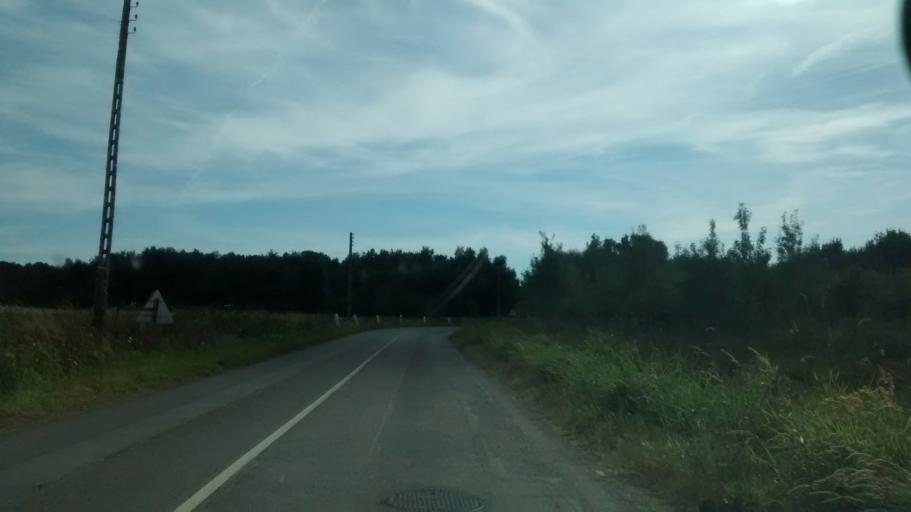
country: FR
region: Pays de la Loire
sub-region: Departement de la Loire-Atlantique
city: Pont-Saint-Martin
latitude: 47.1356
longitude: -1.6110
